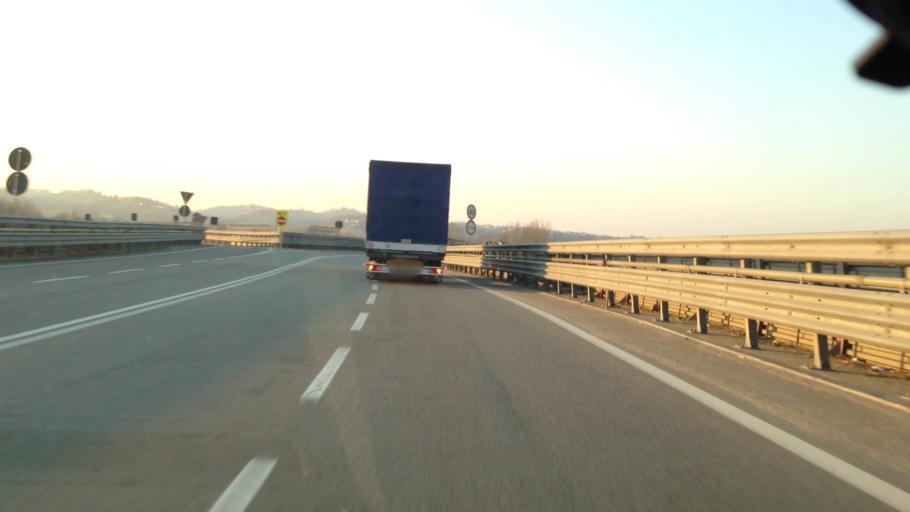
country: IT
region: Piedmont
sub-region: Provincia di Asti
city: Isola d'Asti
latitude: 44.8436
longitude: 8.1909
